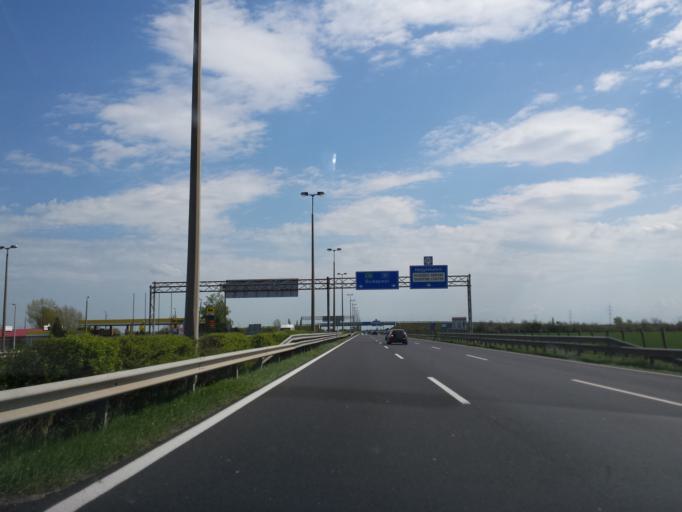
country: AT
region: Burgenland
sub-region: Politischer Bezirk Neusiedl am See
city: Nickelsdorf
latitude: 47.9188
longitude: 17.1202
